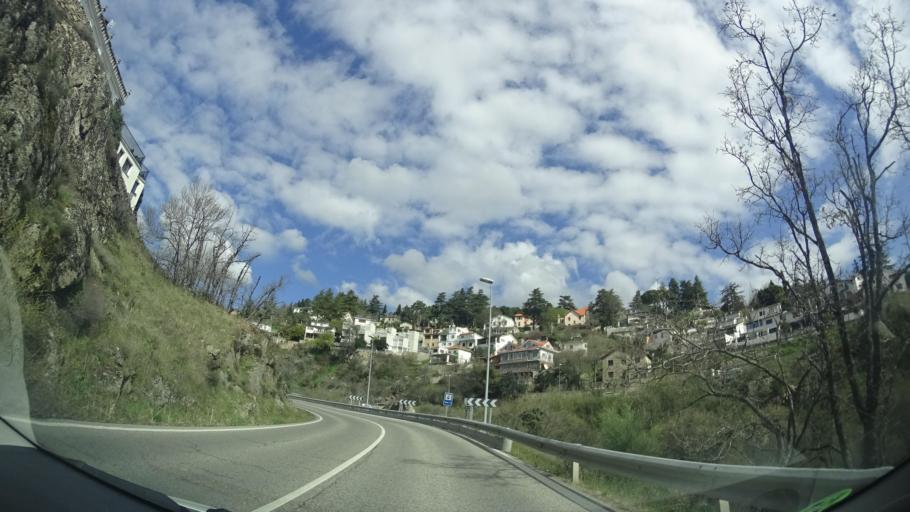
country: ES
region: Madrid
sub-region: Provincia de Madrid
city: Miraflores de la Sierra
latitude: 40.8093
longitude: -3.7724
